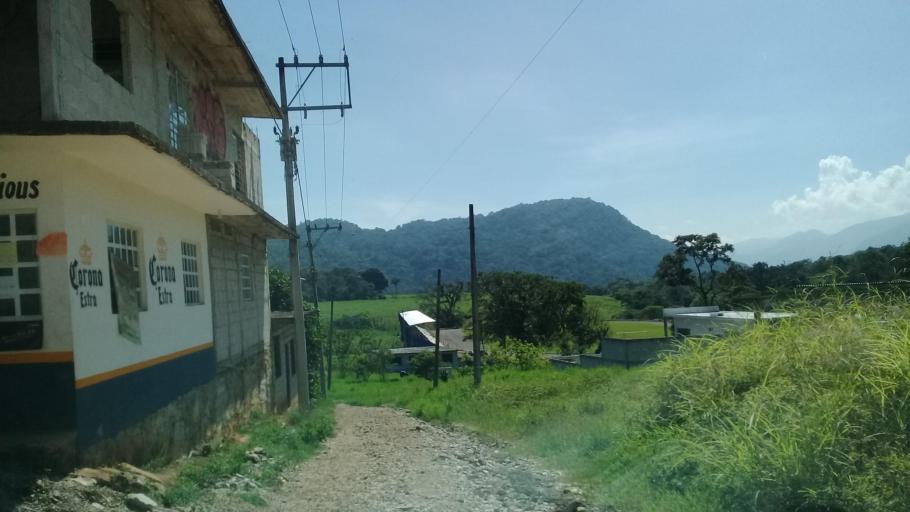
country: MX
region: Veracruz
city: Amatlan de los Reyes
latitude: 18.8441
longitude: -96.9111
